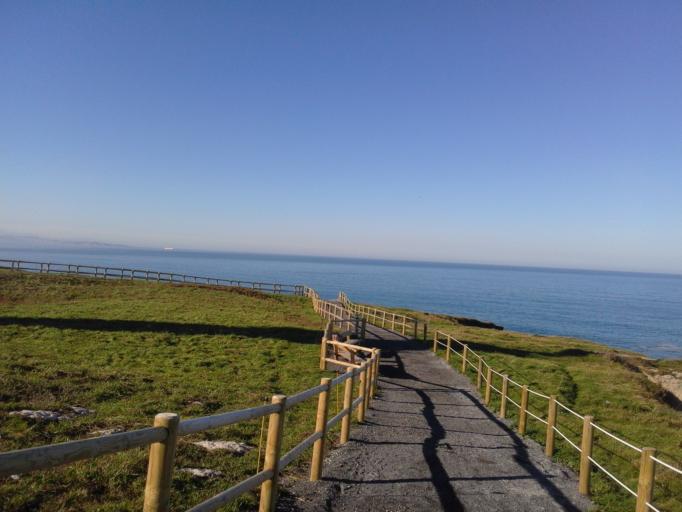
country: ES
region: Cantabria
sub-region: Provincia de Cantabria
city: Arnuero
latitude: 43.5118
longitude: -3.5950
